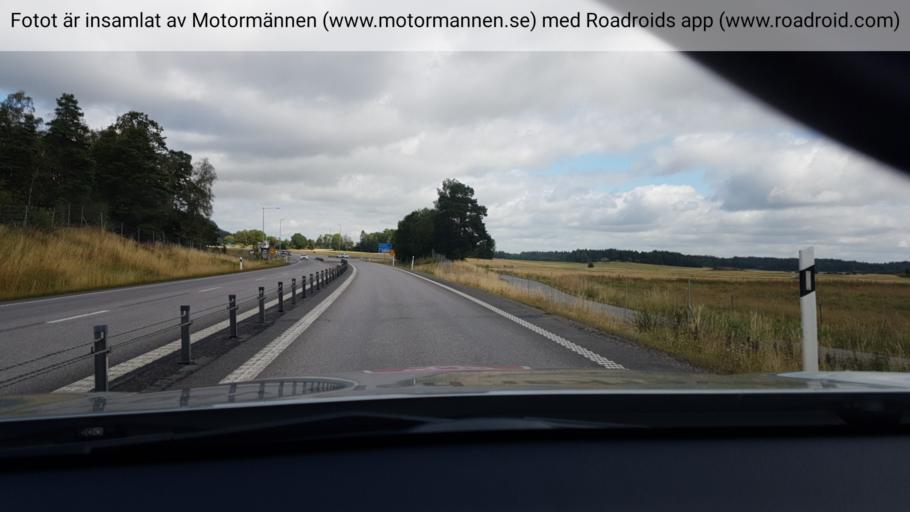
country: SE
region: Vaestra Goetaland
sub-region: Vanersborgs Kommun
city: Vargon
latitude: 58.2928
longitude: 12.4994
